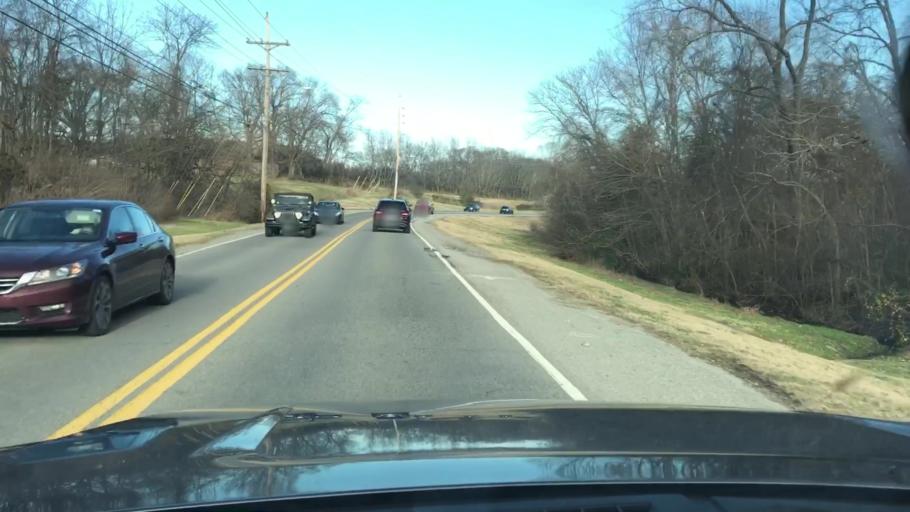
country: US
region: Tennessee
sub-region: Williamson County
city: Brentwood Estates
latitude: 35.9647
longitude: -86.7832
